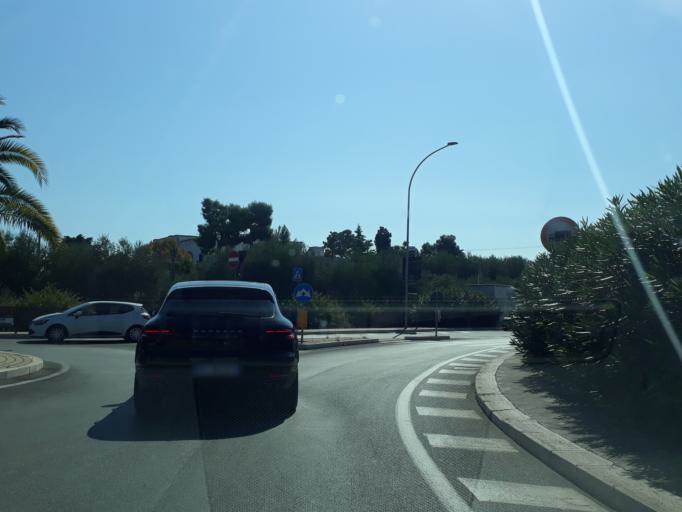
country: IT
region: Apulia
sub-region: Provincia di Bari
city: Monopoli
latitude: 40.9463
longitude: 17.2938
